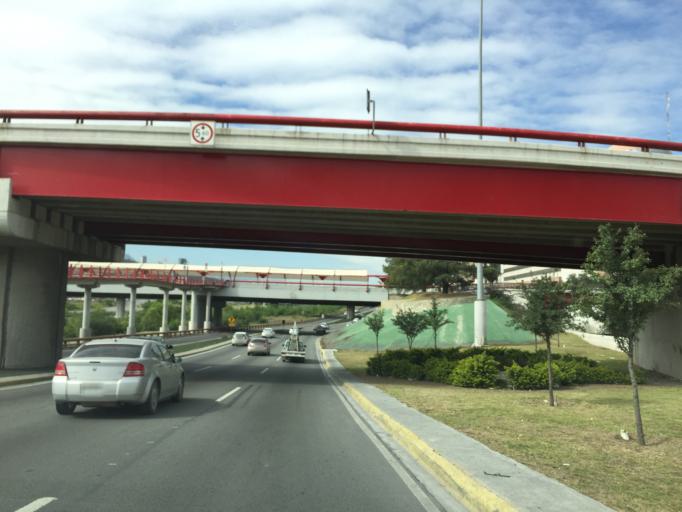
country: MX
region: Nuevo Leon
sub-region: Monterrey
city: Monterrey
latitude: 25.6633
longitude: -100.3099
